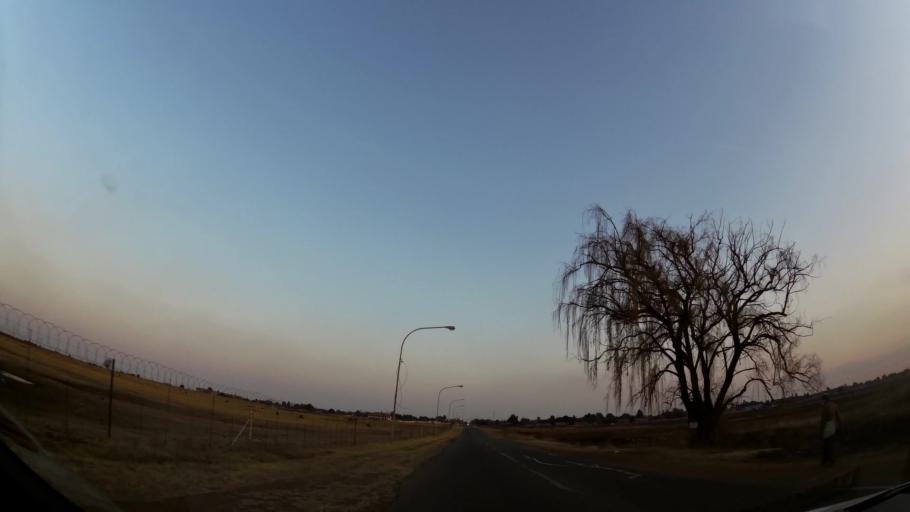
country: ZA
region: Gauteng
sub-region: Ekurhuleni Metropolitan Municipality
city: Springs
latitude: -26.3381
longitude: 28.4359
